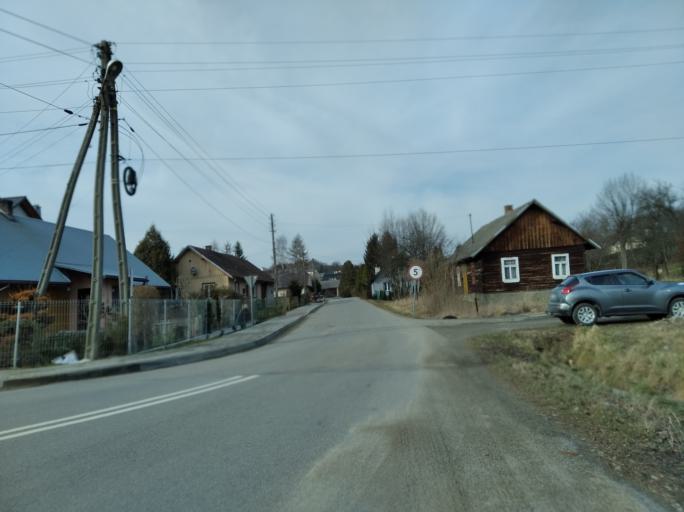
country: PL
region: Subcarpathian Voivodeship
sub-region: Powiat brzozowski
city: Turze Pole
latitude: 49.6624
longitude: 22.0035
